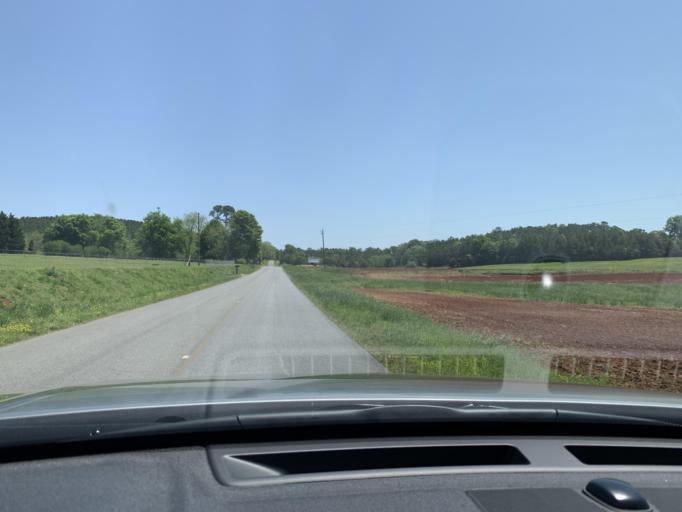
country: US
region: Georgia
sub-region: Polk County
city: Cedartown
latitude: 34.0654
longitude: -85.1661
